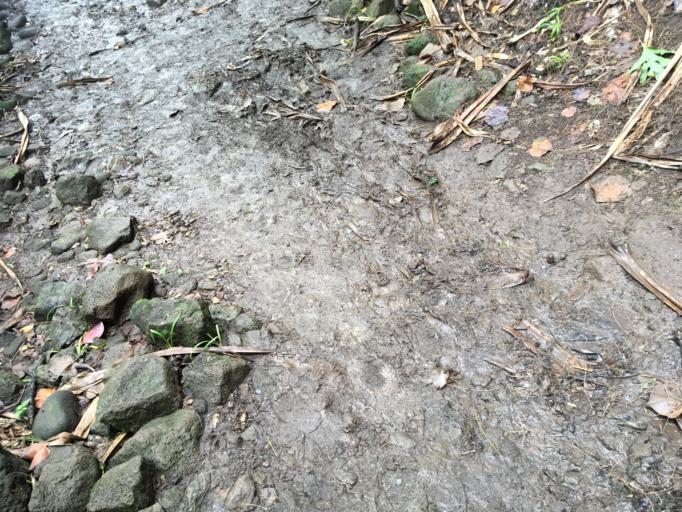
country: US
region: Hawaii
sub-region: Hawaii County
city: Kapaau
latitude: 20.2042
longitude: -155.7319
